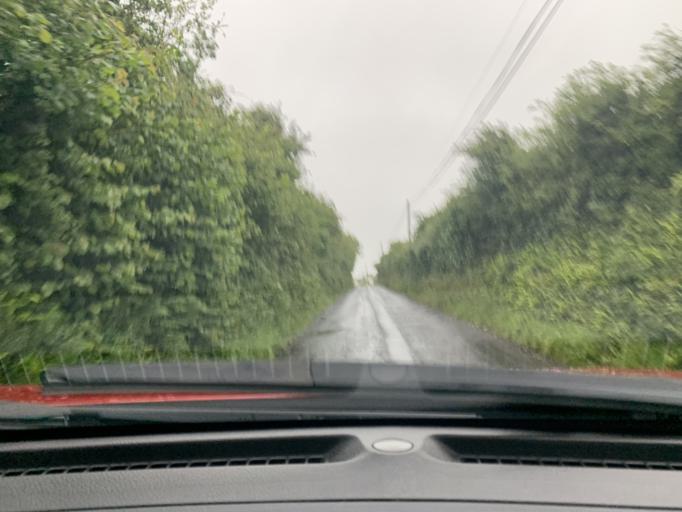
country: IE
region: Connaught
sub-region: County Leitrim
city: Kinlough
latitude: 54.4433
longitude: -8.4405
